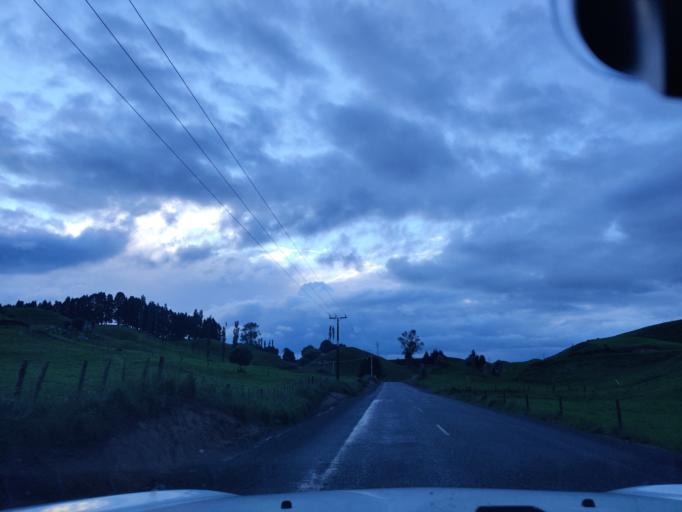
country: NZ
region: Waikato
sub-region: South Waikato District
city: Tokoroa
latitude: -38.1999
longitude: 175.8094
